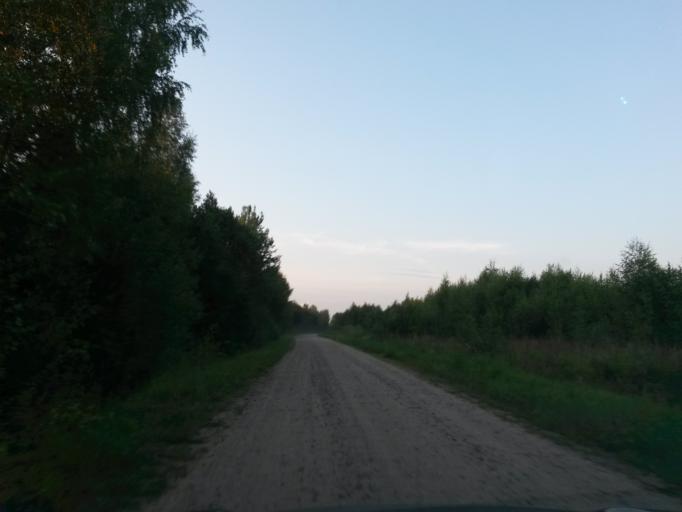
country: RU
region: Jaroslavl
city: Tutayev
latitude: 57.9421
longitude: 39.4472
